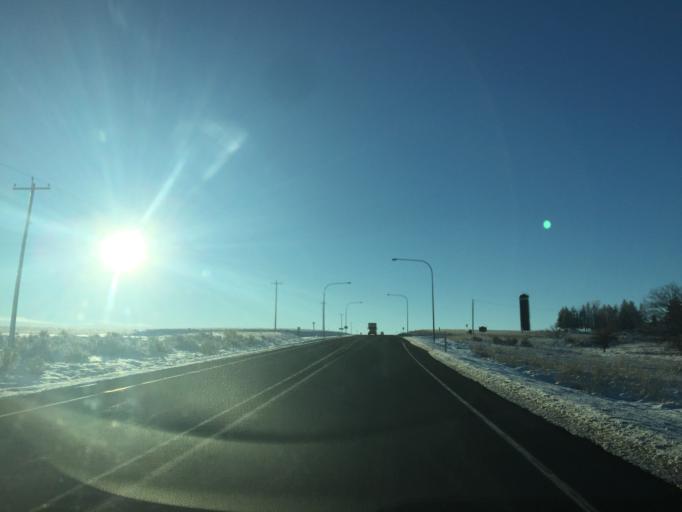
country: US
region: Washington
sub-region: Okanogan County
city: Coulee Dam
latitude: 47.7067
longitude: -118.9371
